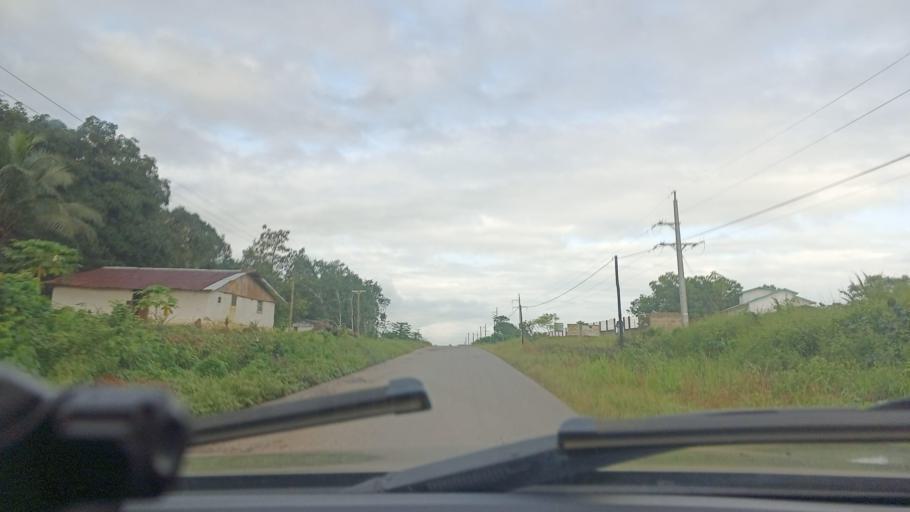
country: LR
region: Montserrado
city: Monrovia
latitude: 6.5689
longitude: -10.8763
